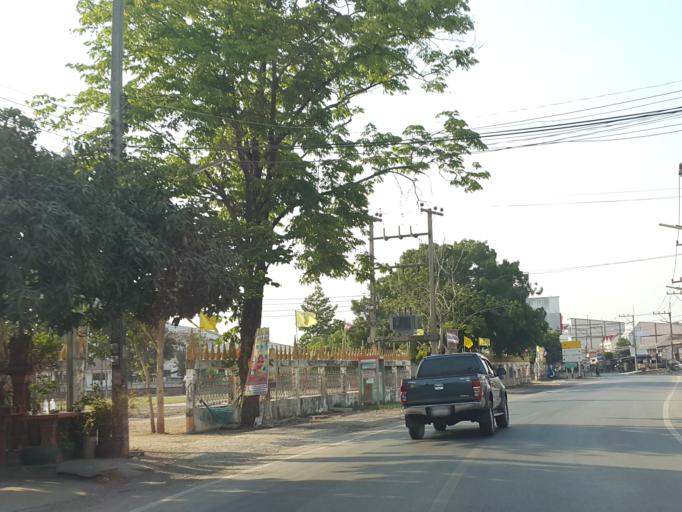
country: TH
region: Phitsanulok
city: Phrom Phiram
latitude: 17.0968
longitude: 100.1685
